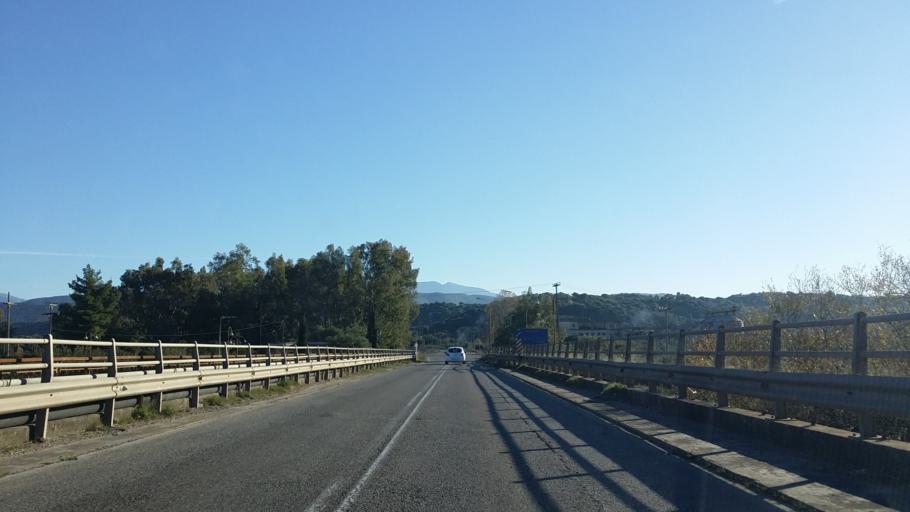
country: GR
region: West Greece
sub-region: Nomos Aitolias kai Akarnanias
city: Neapolis
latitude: 38.6699
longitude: 21.3396
